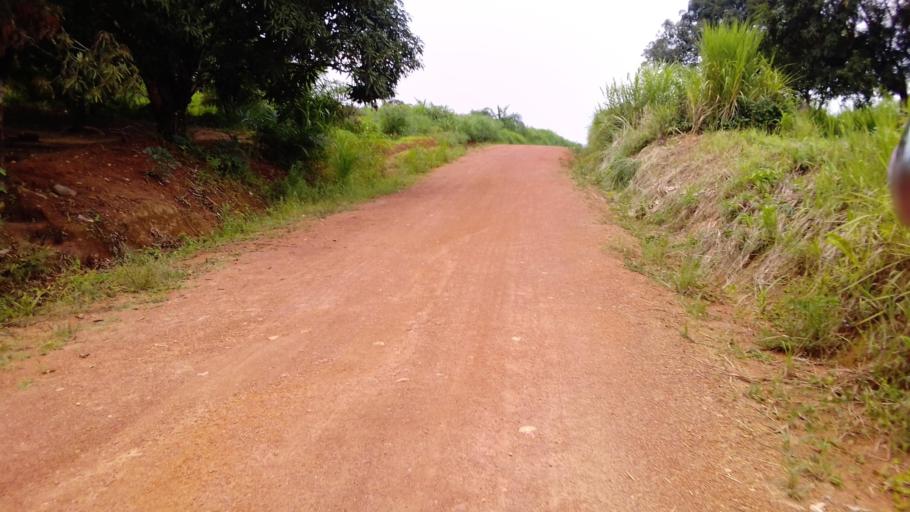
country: SL
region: Eastern Province
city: Koidu
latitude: 8.6624
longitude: -10.9415
